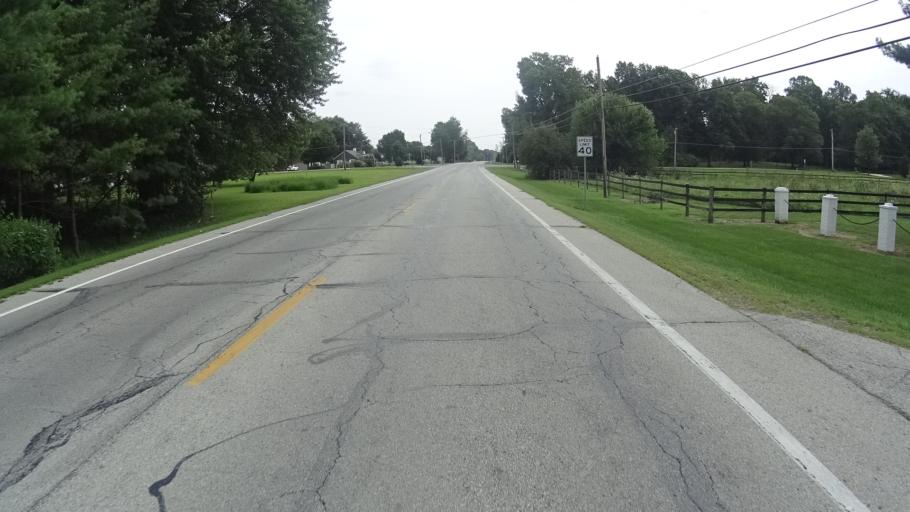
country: US
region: Indiana
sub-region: Madison County
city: Edgewood
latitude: 40.1015
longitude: -85.7506
